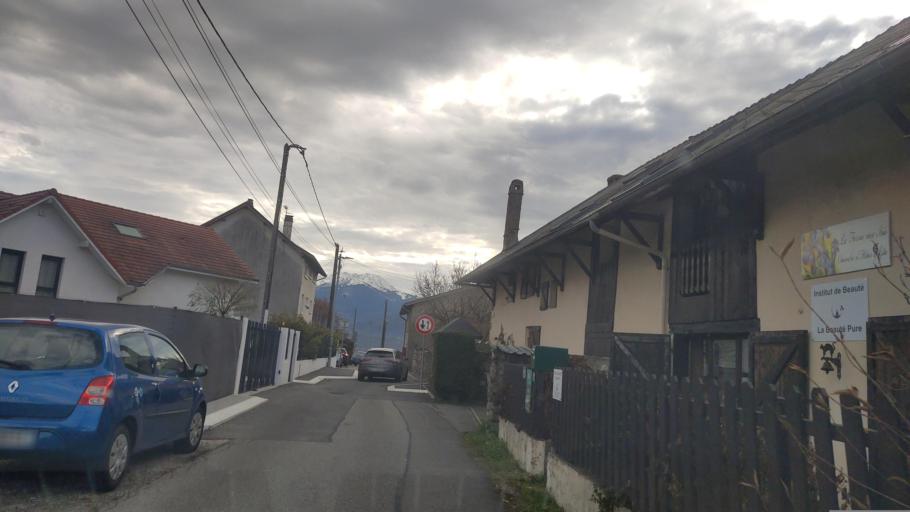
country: FR
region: Rhone-Alpes
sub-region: Departement de la Savoie
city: Les Marches
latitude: 45.5016
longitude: 6.0067
